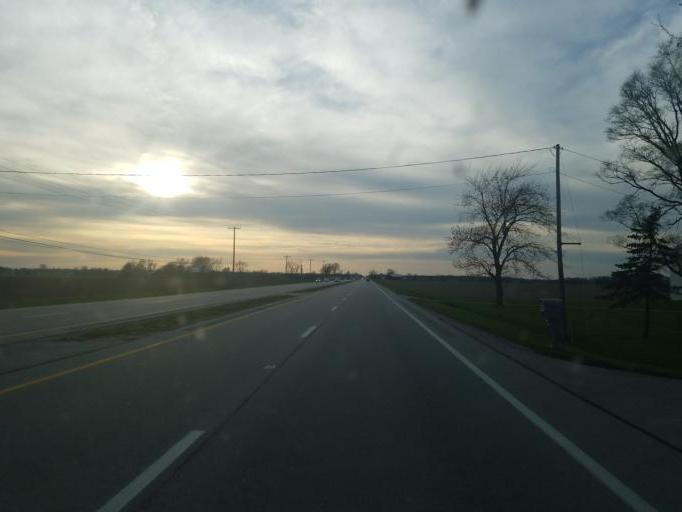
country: US
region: Ohio
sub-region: Sandusky County
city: Gibsonburg
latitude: 41.4177
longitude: -83.2820
